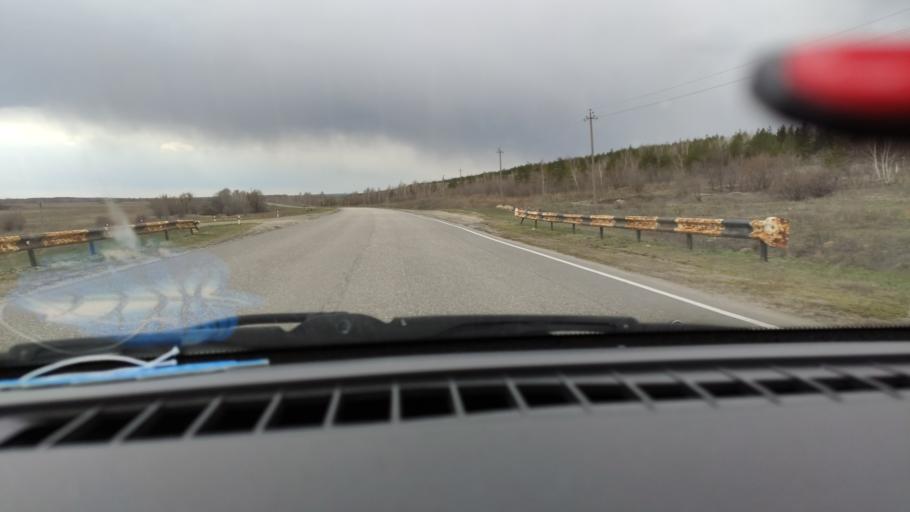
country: RU
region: Saratov
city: Sinodskoye
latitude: 52.0630
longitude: 46.7664
